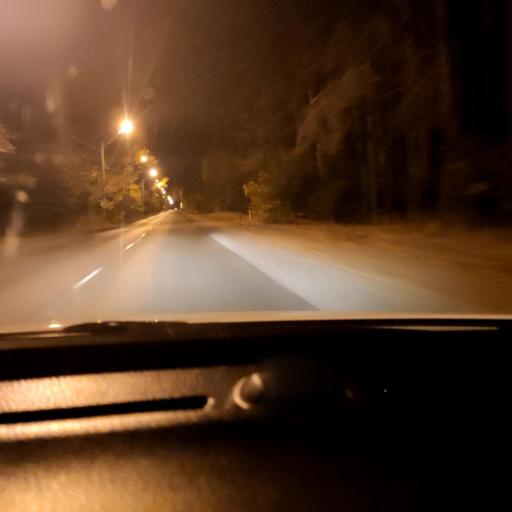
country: RU
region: Voronezj
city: Somovo
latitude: 51.7063
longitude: 39.3252
